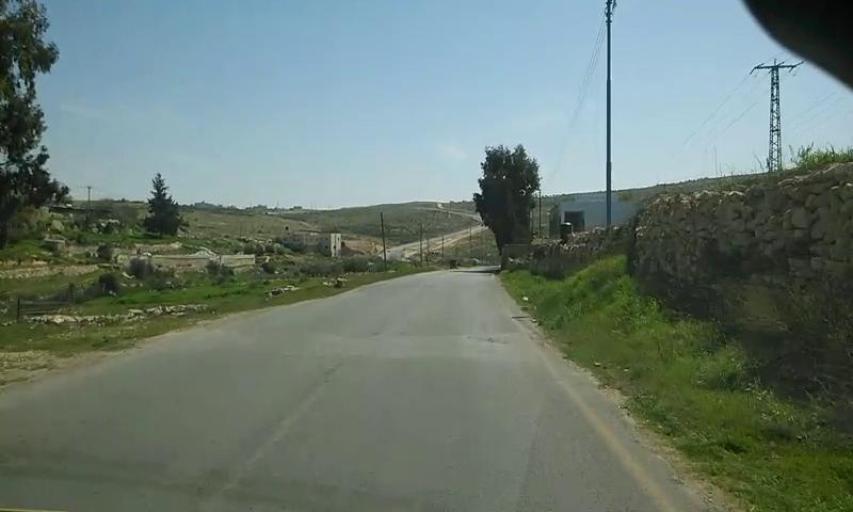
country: PS
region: West Bank
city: Marah Rabbah
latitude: 31.6286
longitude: 35.2064
